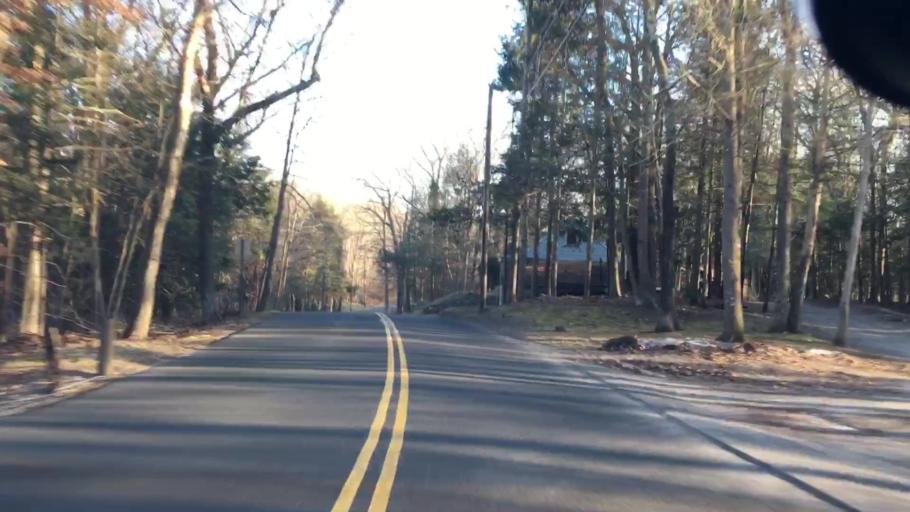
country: US
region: Connecticut
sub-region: Fairfield County
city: Newtown
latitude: 41.4684
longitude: -73.3384
